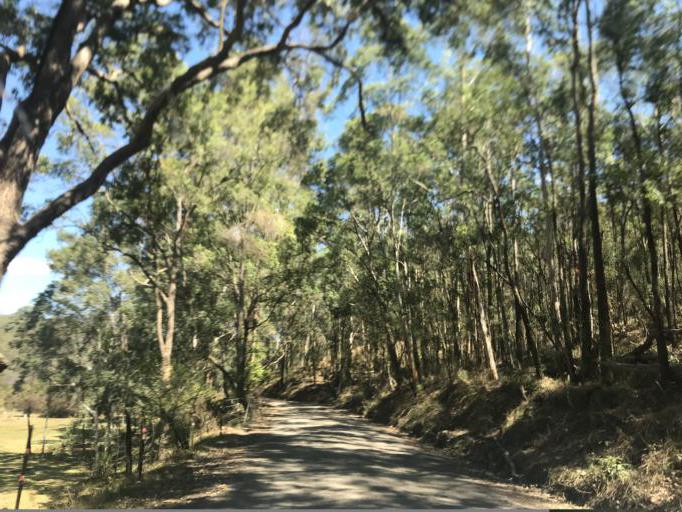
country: AU
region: New South Wales
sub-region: Wyong Shire
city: Little Jilliby
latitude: -33.1992
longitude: 150.9988
